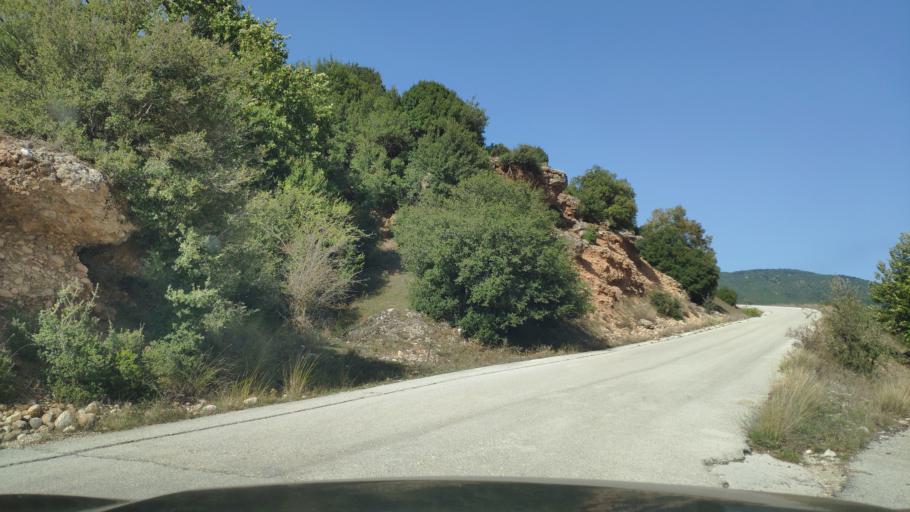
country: GR
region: West Greece
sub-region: Nomos Achaias
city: Aiyira
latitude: 37.9846
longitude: 22.3581
